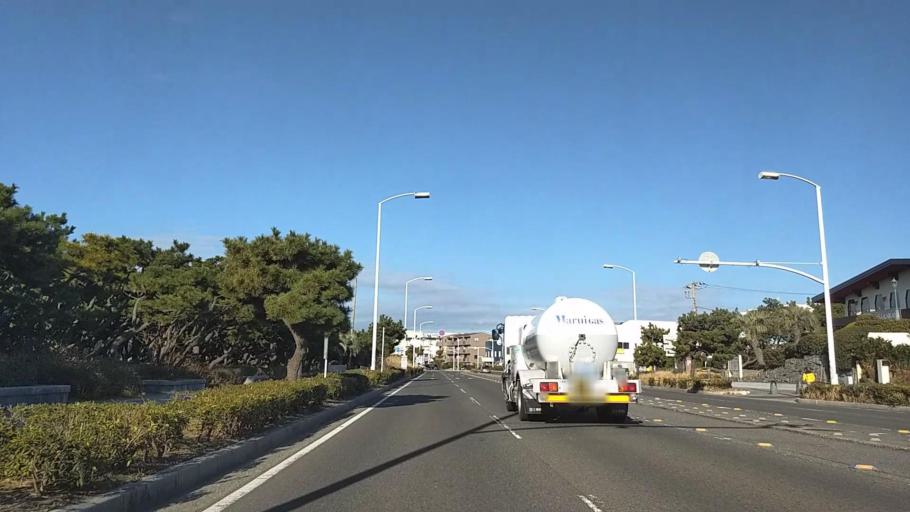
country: JP
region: Kanagawa
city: Fujisawa
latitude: 35.3159
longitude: 139.4725
